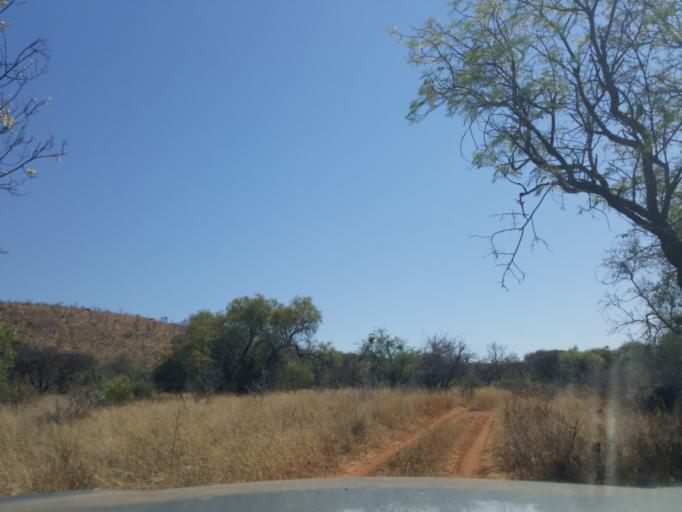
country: BW
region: South East
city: Lobatse
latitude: -25.1443
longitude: 25.6695
